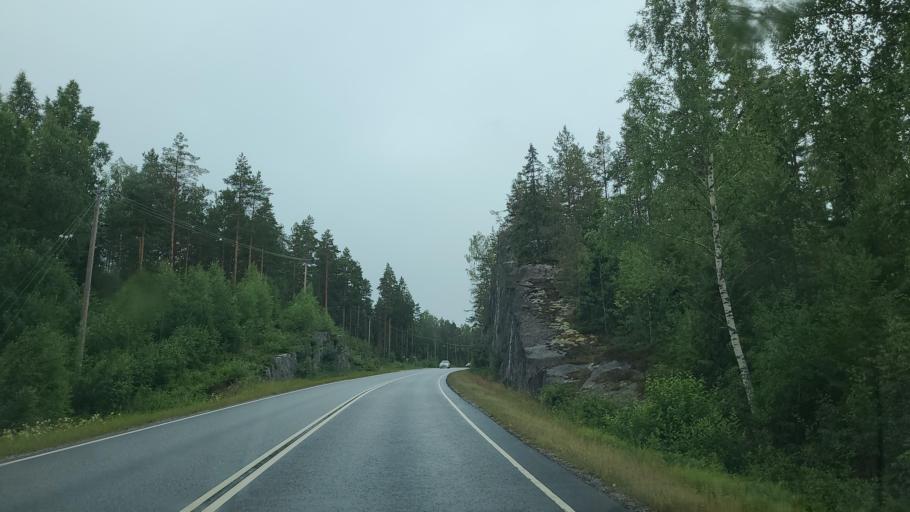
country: FI
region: Varsinais-Suomi
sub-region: Turku
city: Sauvo
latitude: 60.2715
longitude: 22.6688
